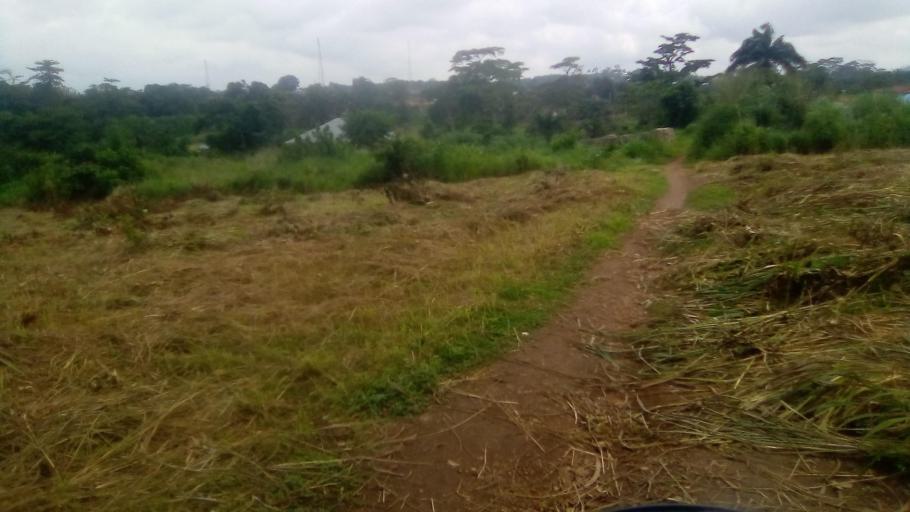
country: SL
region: Eastern Province
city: Kailahun
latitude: 8.2712
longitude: -10.5661
